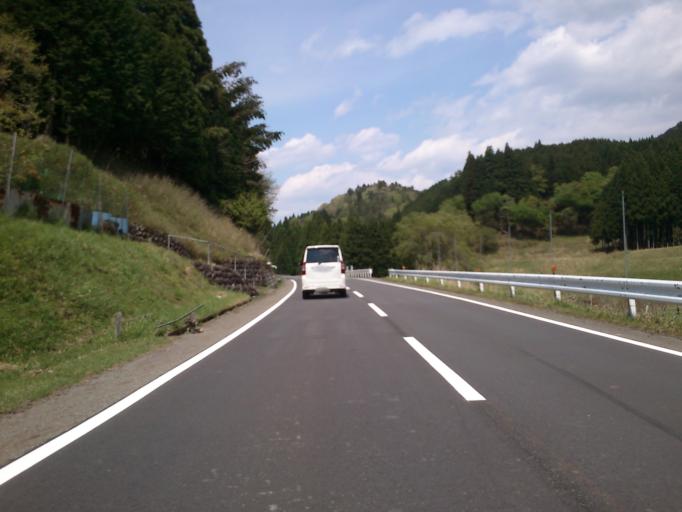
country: JP
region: Hyogo
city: Toyooka
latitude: 35.4017
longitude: 134.9478
